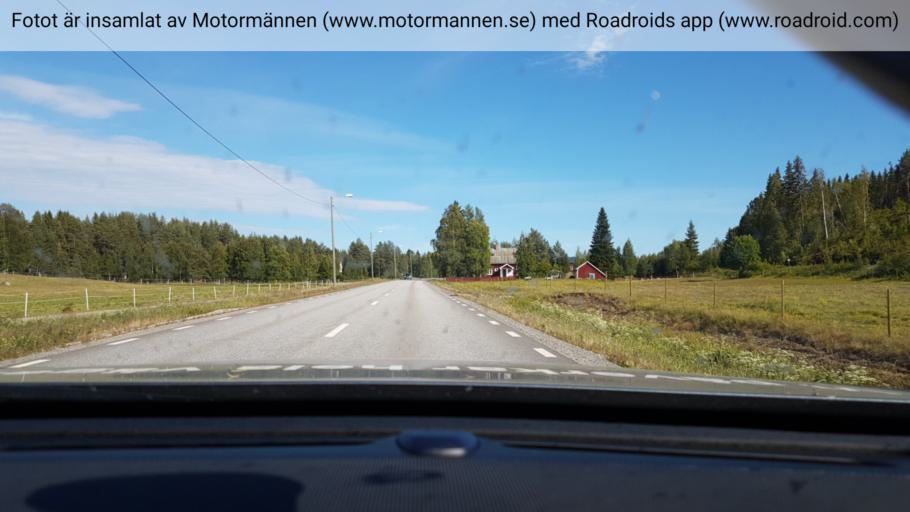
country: SE
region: Vaesterbotten
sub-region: Lycksele Kommun
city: Lycksele
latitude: 64.6972
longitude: 18.3794
